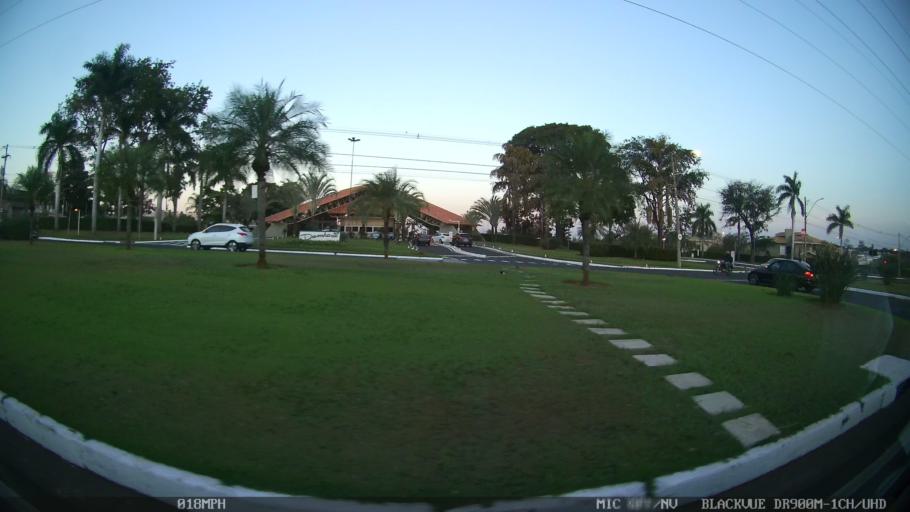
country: BR
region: Sao Paulo
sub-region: Sao Jose Do Rio Preto
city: Sao Jose do Rio Preto
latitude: -20.8223
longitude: -49.3408
